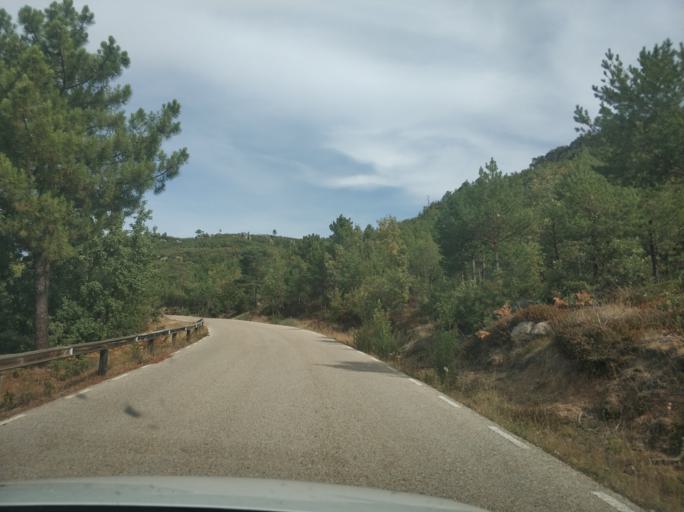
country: ES
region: Castille and Leon
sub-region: Provincia de Soria
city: Duruelo de la Sierra
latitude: 41.9032
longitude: -2.9415
